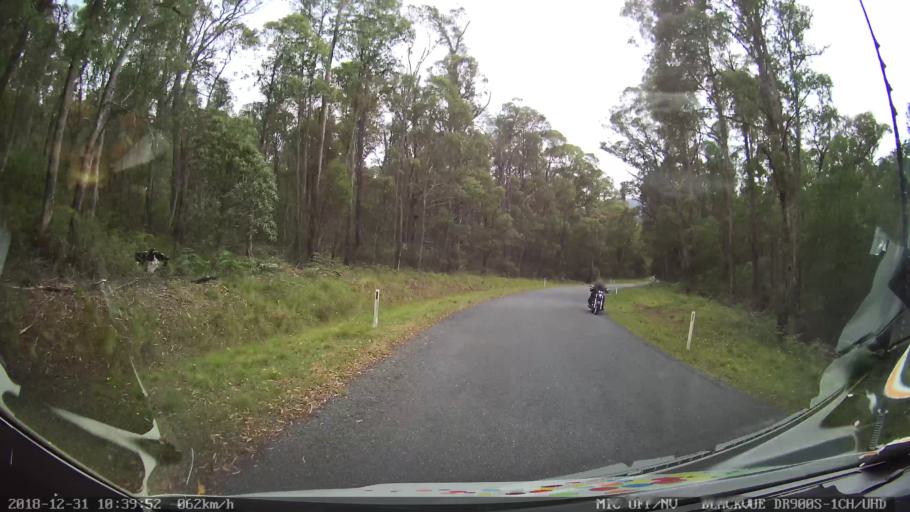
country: AU
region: New South Wales
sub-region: Snowy River
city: Jindabyne
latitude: -36.3946
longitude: 148.1775
